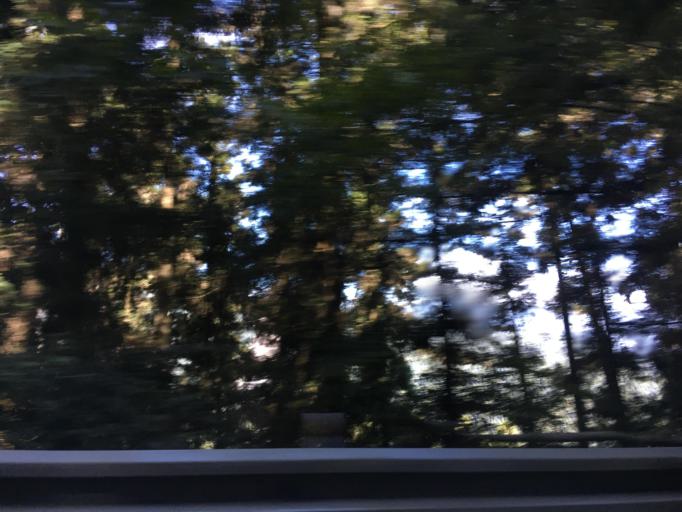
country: TW
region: Taiwan
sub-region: Yilan
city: Yilan
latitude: 24.5403
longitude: 121.5123
